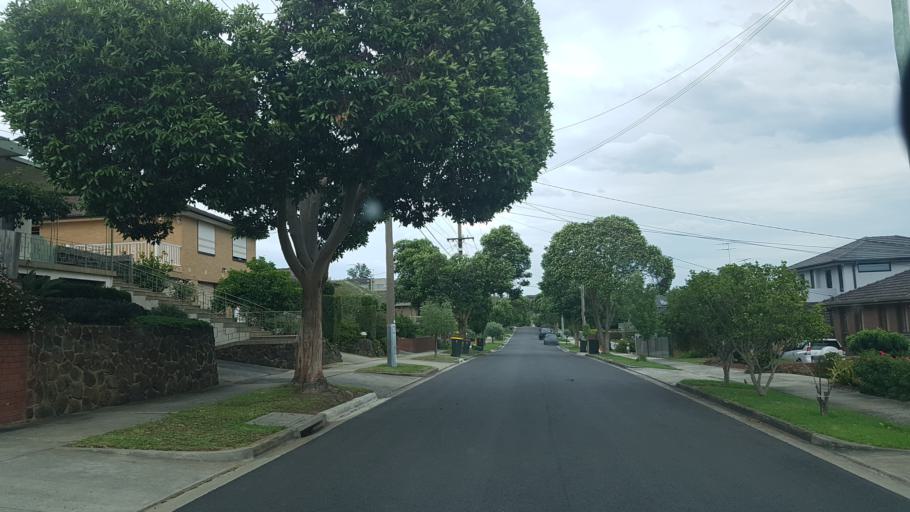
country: AU
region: Victoria
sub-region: Manningham
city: Bulleen
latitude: -37.7615
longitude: 145.0871
